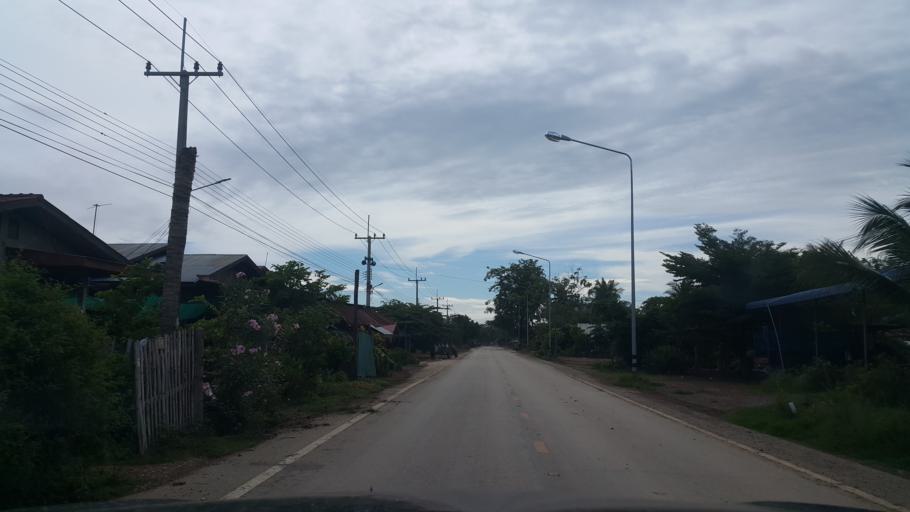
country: TH
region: Sukhothai
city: Si Nakhon
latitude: 17.2738
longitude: 99.9860
